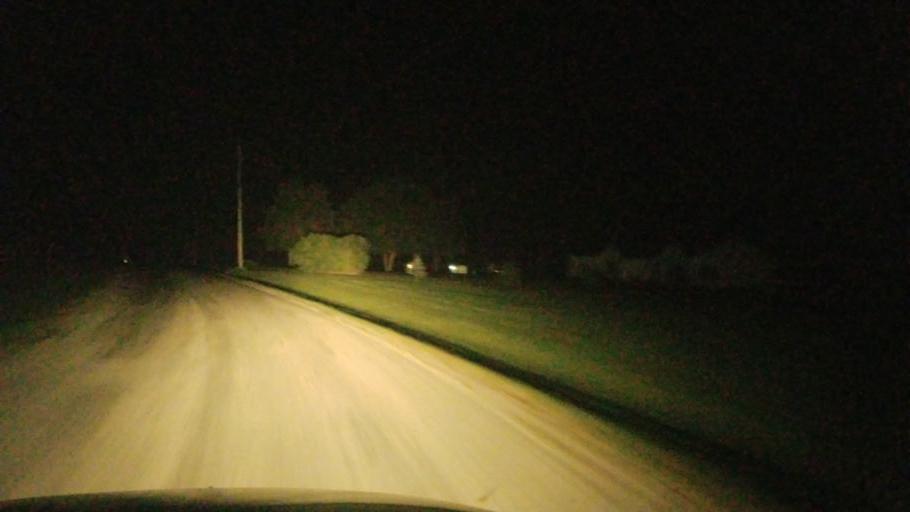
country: US
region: Ohio
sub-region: Highland County
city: Leesburg
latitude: 39.2985
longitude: -83.5567
